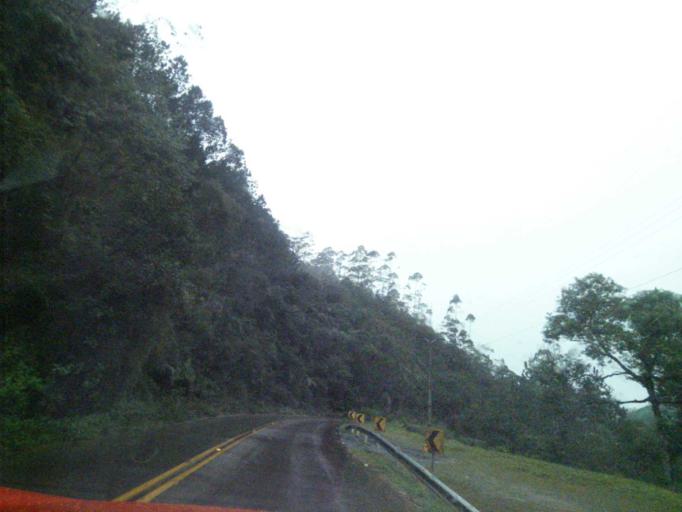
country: BR
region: Santa Catarina
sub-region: Anitapolis
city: Anitapolis
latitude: -27.8368
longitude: -49.0519
